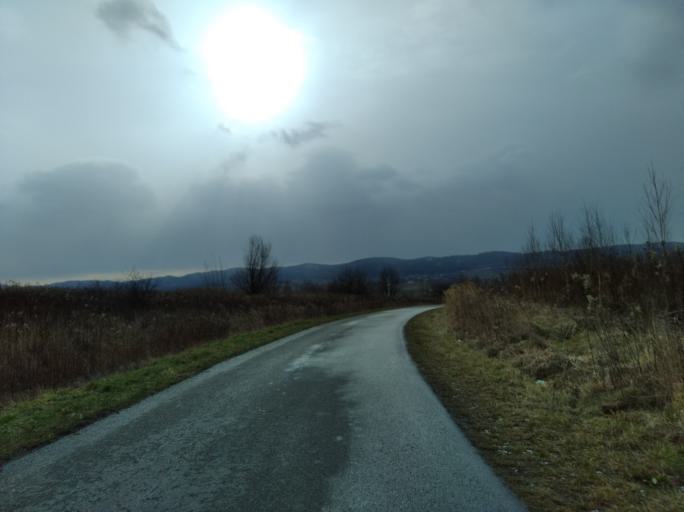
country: PL
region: Subcarpathian Voivodeship
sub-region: Powiat strzyzowski
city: Wysoka Strzyzowska
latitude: 49.8834
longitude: 21.7274
